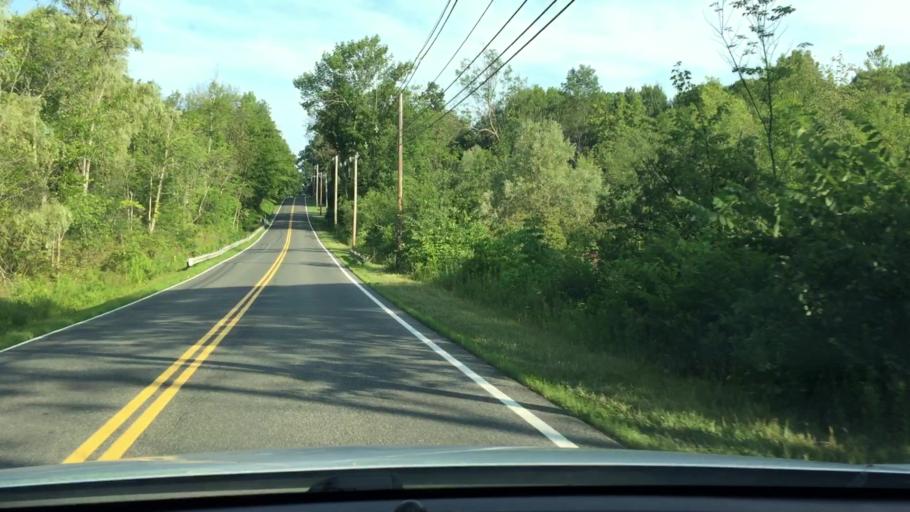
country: US
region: Massachusetts
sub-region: Berkshire County
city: Lenox
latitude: 42.3411
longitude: -73.2581
